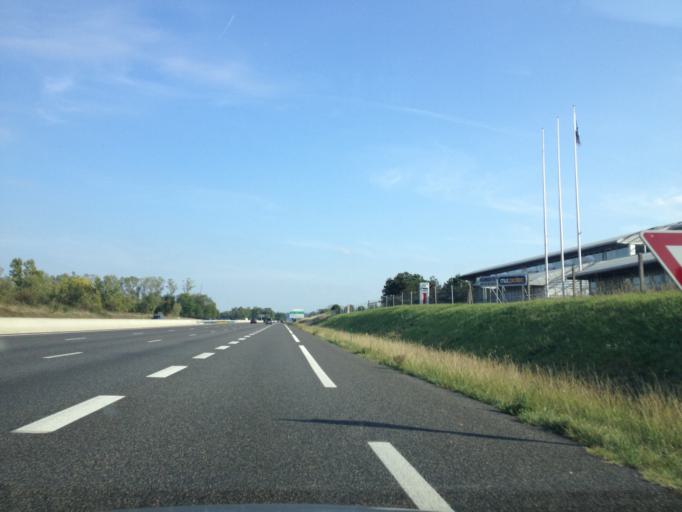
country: FR
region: Rhone-Alpes
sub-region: Departement de l'Isere
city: Vaulx-Milieu
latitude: 45.6288
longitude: 5.1680
